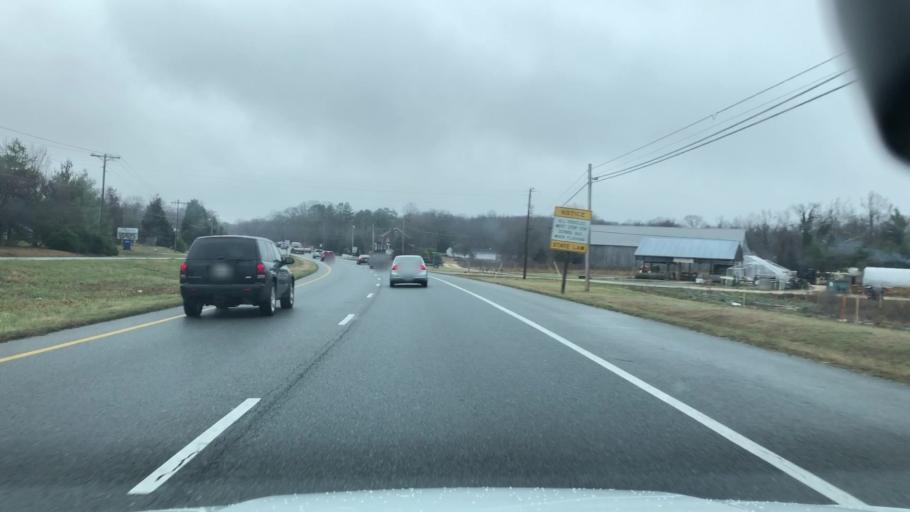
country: US
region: Maryland
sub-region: Charles County
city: Saint Charles
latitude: 38.5839
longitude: -76.8616
